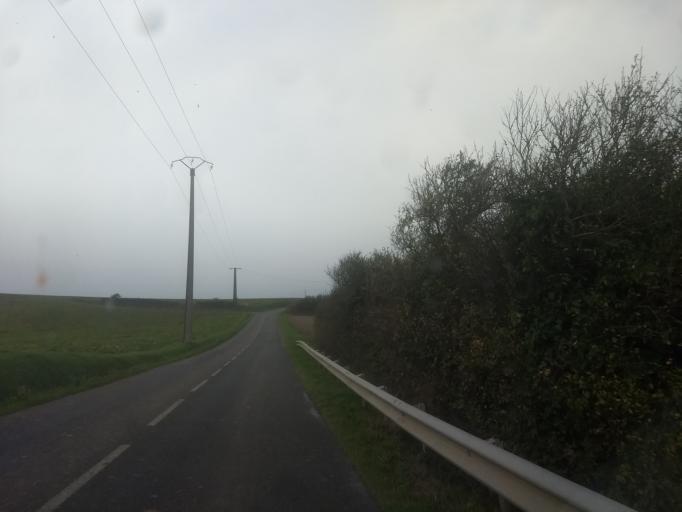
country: FR
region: Nord-Pas-de-Calais
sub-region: Departement du Pas-de-Calais
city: Wissant
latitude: 50.8898
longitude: 1.6887
